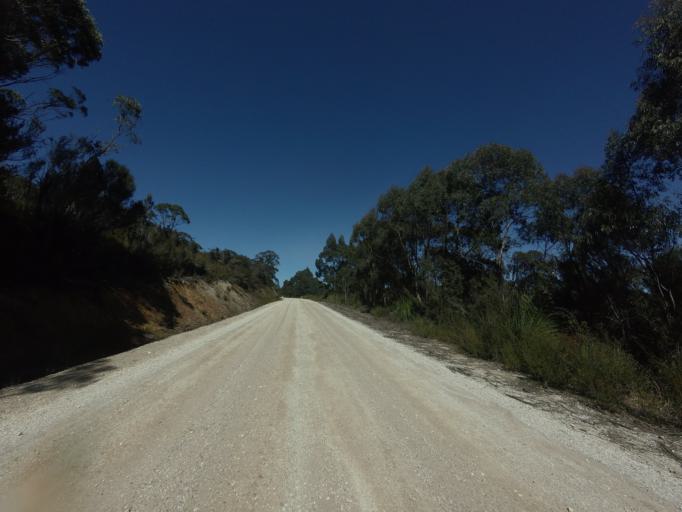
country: AU
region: Tasmania
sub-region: Huon Valley
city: Geeveston
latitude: -42.9093
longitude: 146.3639
